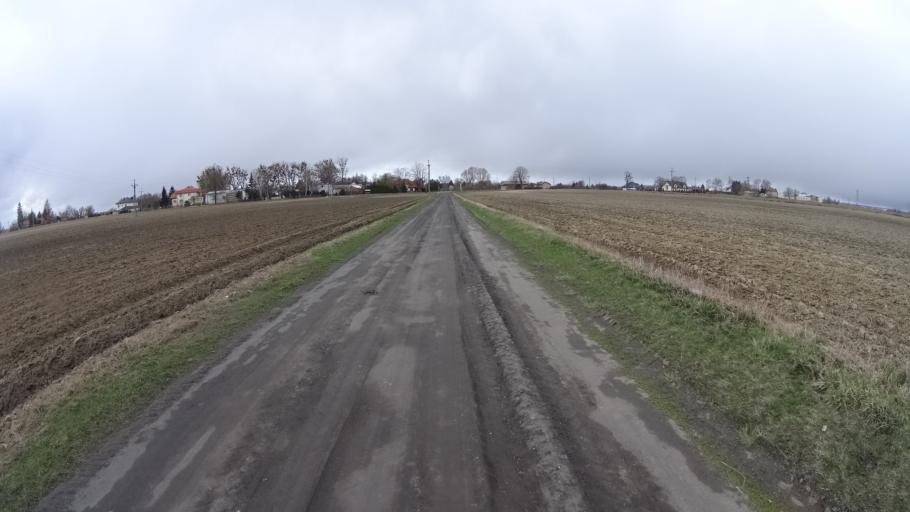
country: PL
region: Masovian Voivodeship
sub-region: Powiat warszawski zachodni
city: Blonie
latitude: 52.2162
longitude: 20.6563
